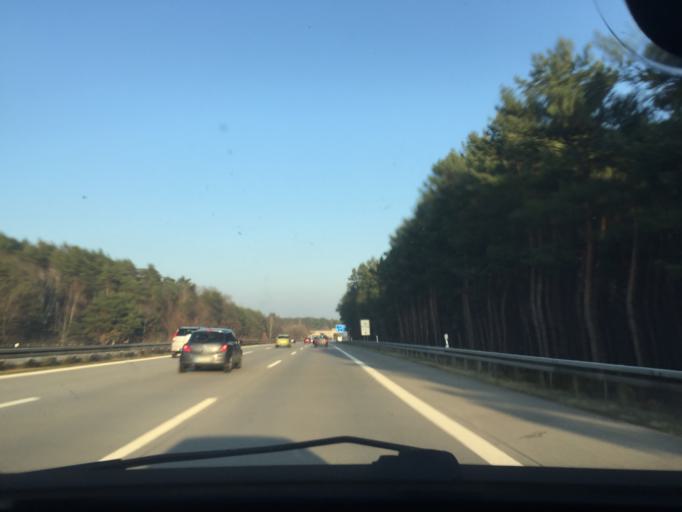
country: DE
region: Brandenburg
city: Michendorf
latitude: 52.3252
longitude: 13.1038
